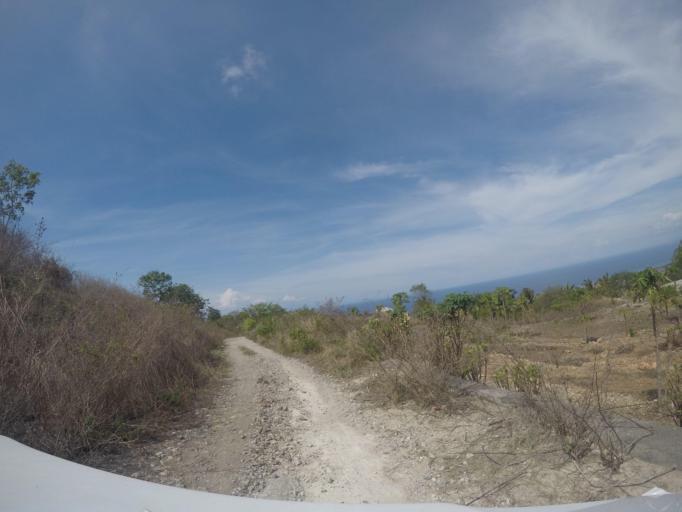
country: TL
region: Baucau
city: Baucau
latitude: -8.4676
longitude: 126.4705
